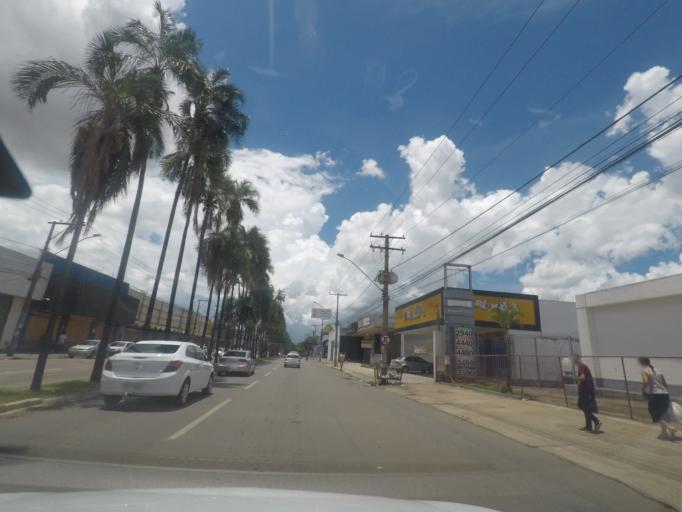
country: BR
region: Goias
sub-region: Goiania
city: Goiania
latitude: -16.6635
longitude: -49.2584
